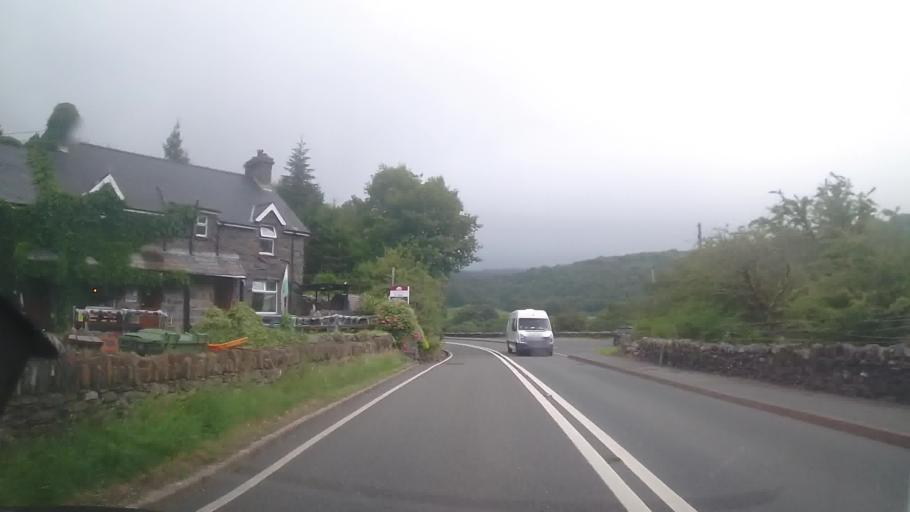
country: GB
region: Wales
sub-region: Conwy
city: Betws-y-Coed
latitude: 53.0954
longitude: -3.8888
